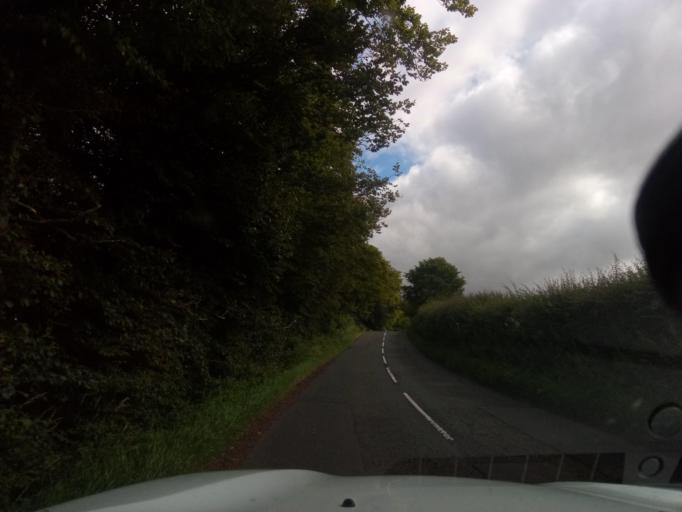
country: GB
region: Scotland
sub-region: The Scottish Borders
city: Newtown St Boswells
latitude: 55.6082
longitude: -2.6612
